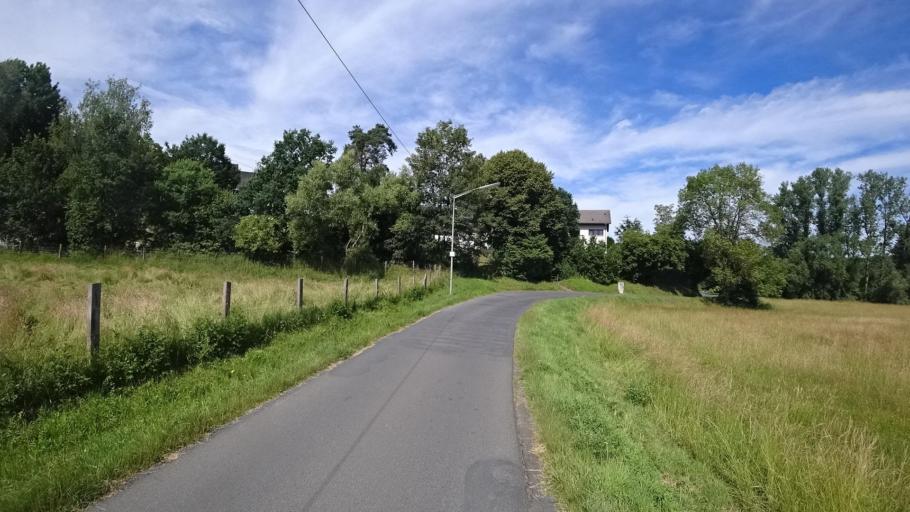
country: DE
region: Rheinland-Pfalz
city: Schoneberg
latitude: 50.6655
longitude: 7.5909
